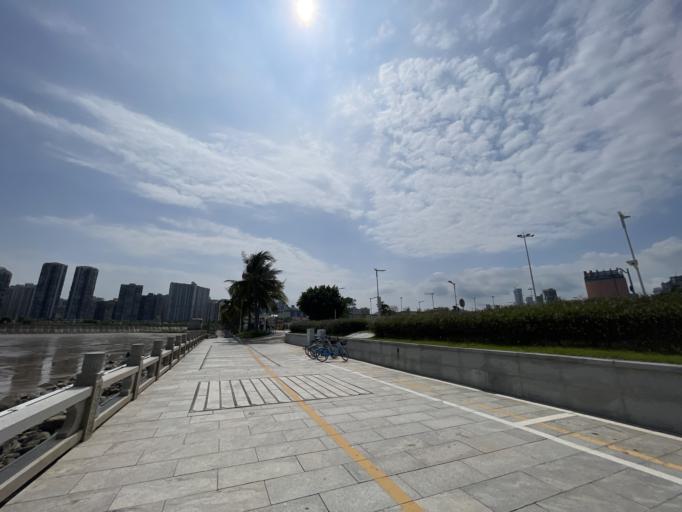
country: MO
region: Macau
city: Macau
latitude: 22.2201
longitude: 113.5535
